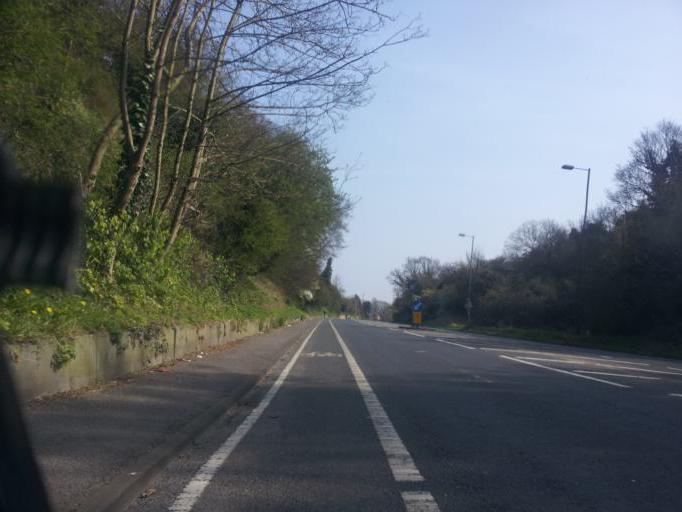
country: GB
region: England
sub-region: Kent
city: Strood
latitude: 51.4062
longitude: 0.4751
